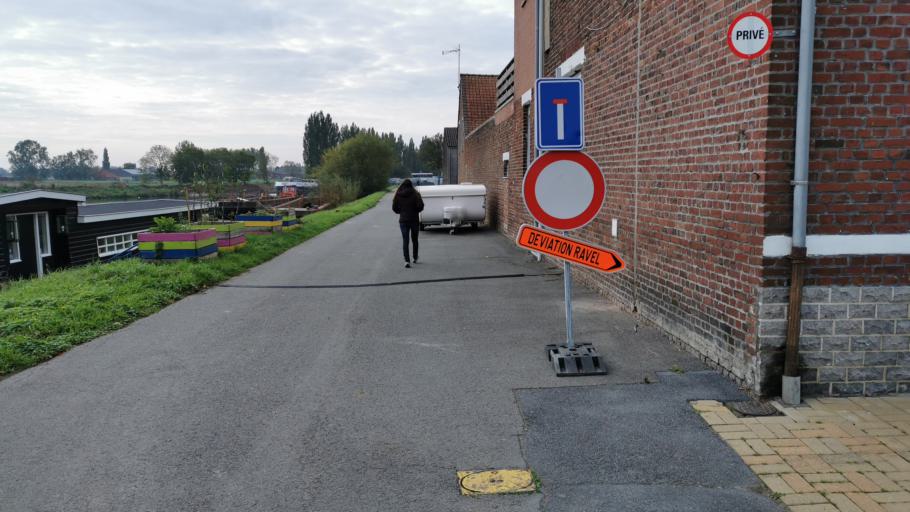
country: FR
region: Nord-Pas-de-Calais
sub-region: Departement du Nord
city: Deulemont
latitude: 50.7504
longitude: 2.9486
